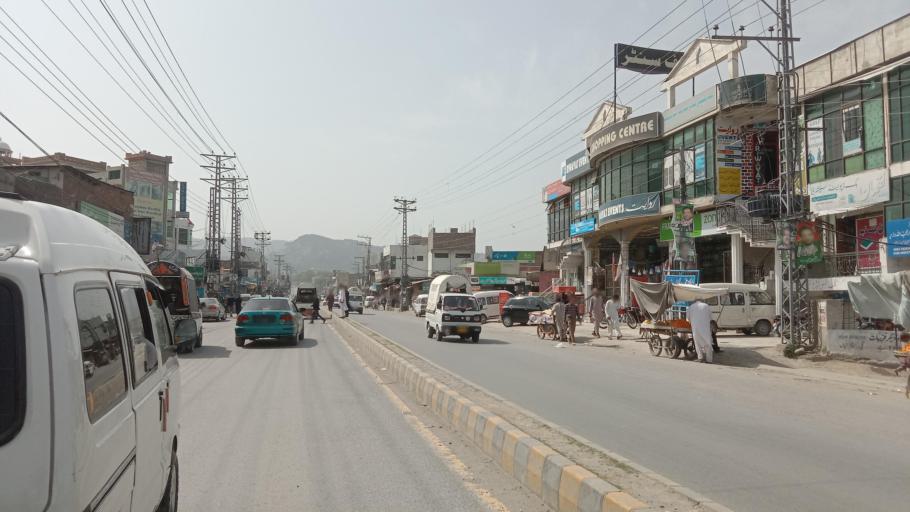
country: PK
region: Khyber Pakhtunkhwa
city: Abbottabad
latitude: 34.1572
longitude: 73.2367
